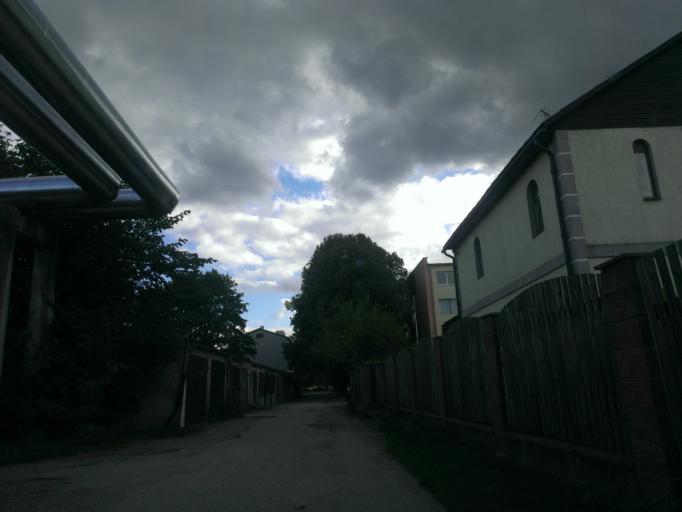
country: LV
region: Sigulda
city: Sigulda
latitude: 57.1550
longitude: 24.8792
